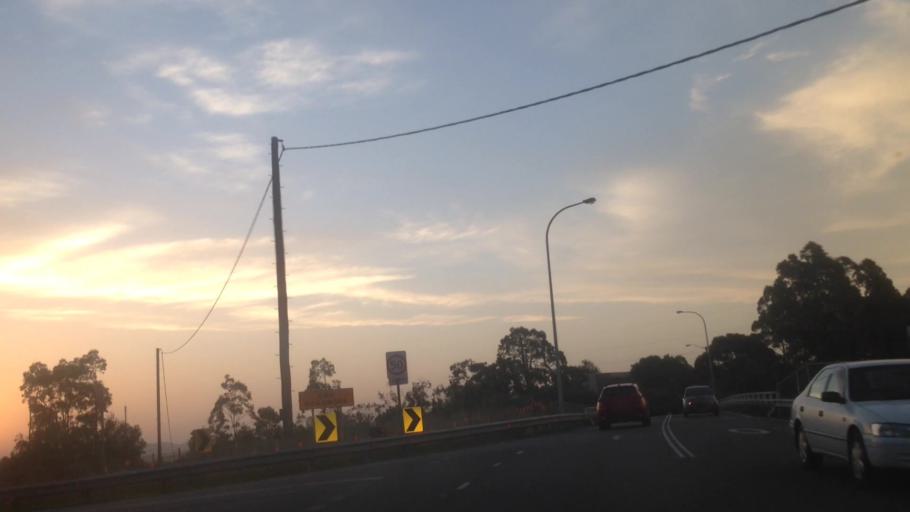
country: AU
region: New South Wales
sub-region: Lake Macquarie Shire
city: Dora Creek
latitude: -33.1075
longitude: 151.4933
